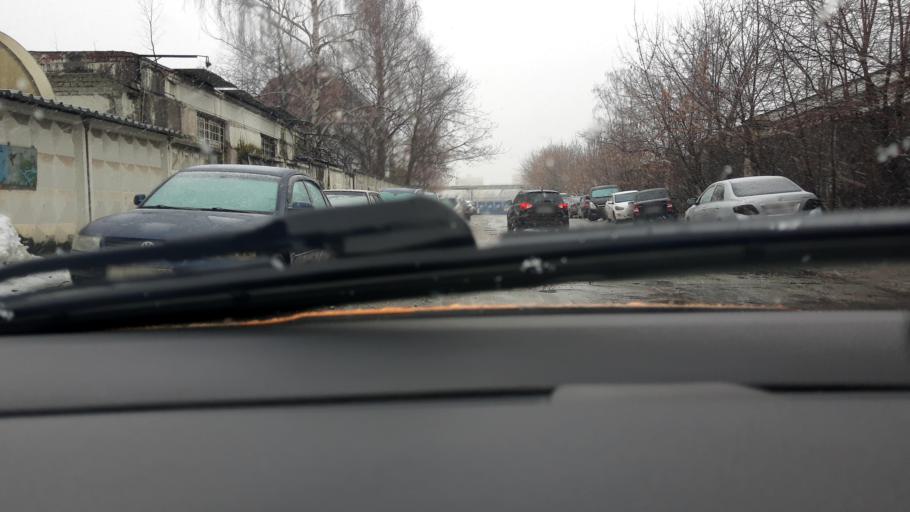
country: RU
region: Moscow
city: Slobodka
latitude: 55.8584
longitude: 37.5824
